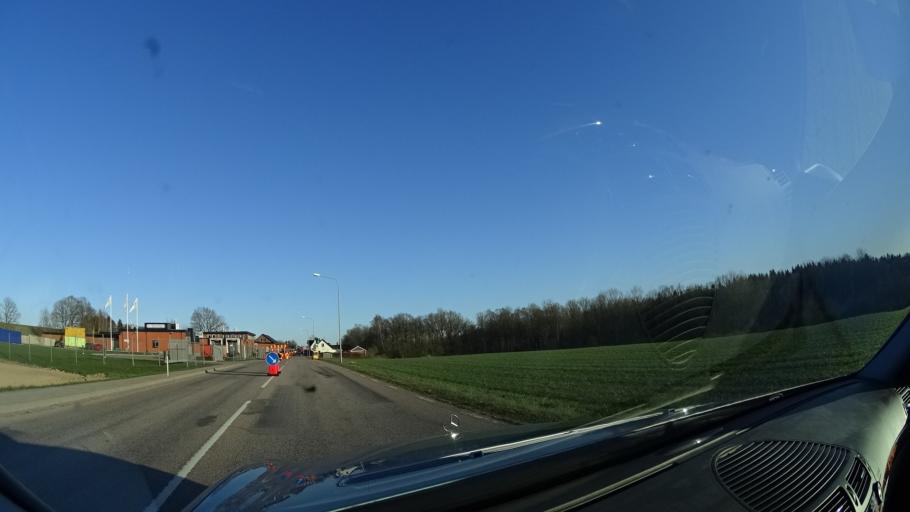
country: SE
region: Skane
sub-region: Bjuvs Kommun
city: Billesholm
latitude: 56.0578
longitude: 12.9927
